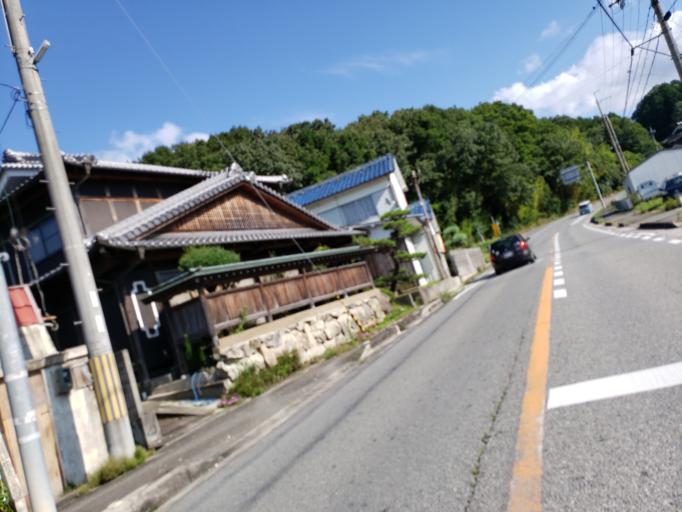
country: JP
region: Hyogo
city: Kakogawacho-honmachi
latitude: 34.8951
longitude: 134.8068
